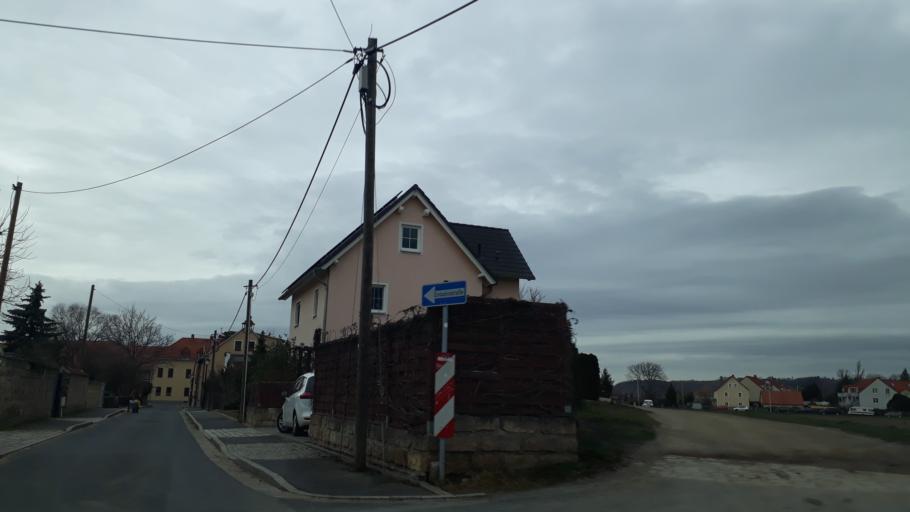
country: DE
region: Saxony
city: Radebeul
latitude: 51.0832
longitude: 13.6739
